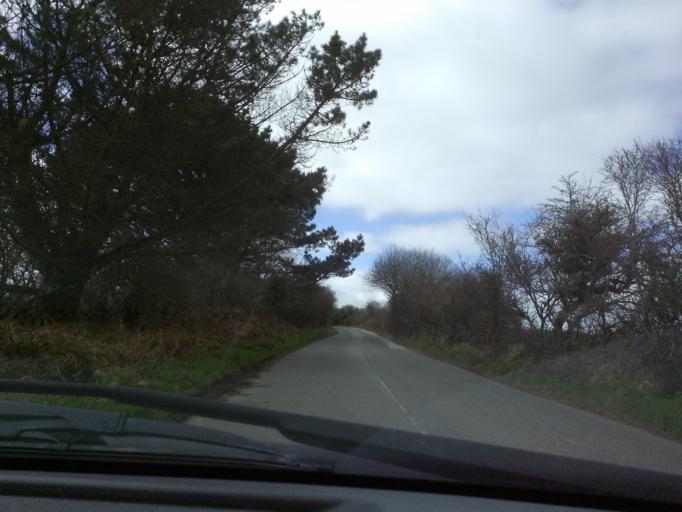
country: GB
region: England
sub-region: Cornwall
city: St. Buryan
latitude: 50.0605
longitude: -5.6274
